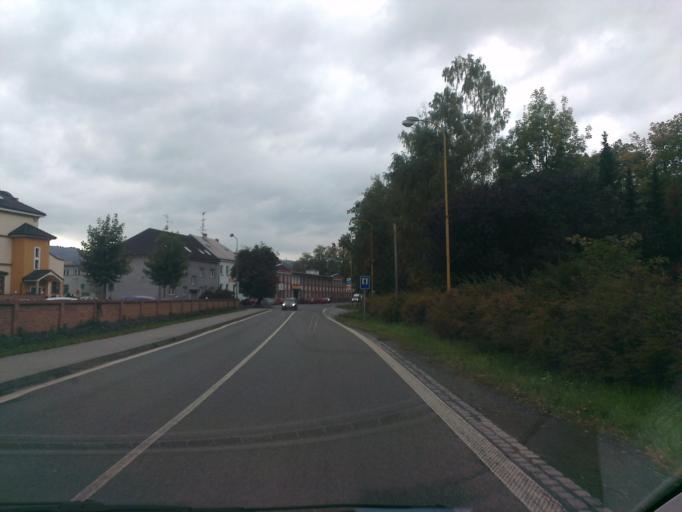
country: CZ
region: Zlin
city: Valasske Mezirici
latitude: 49.4693
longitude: 17.9589
